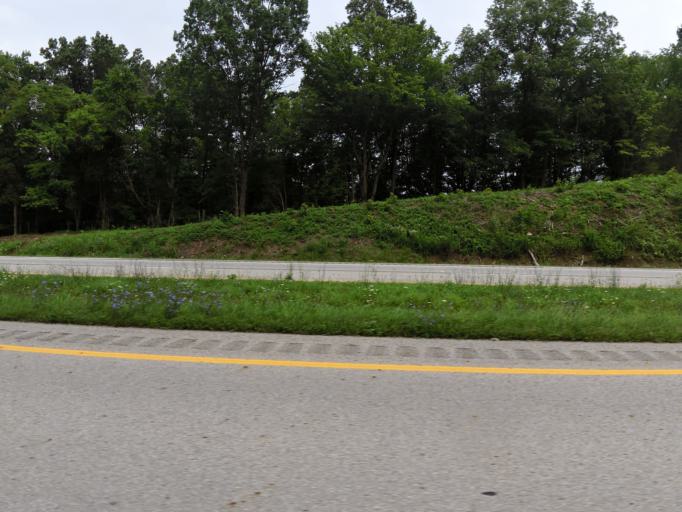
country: US
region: Kentucky
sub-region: Ohio County
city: Beaver Dam
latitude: 37.3532
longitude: -86.9167
